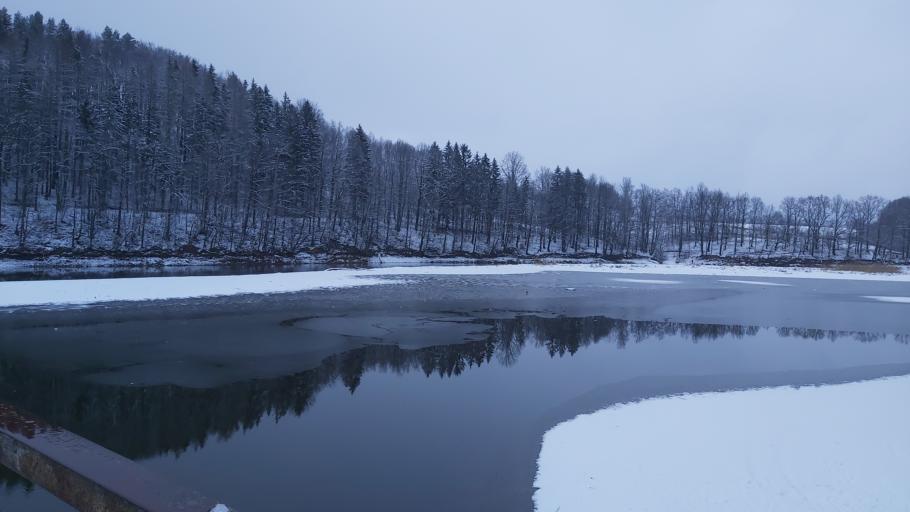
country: PL
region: Lower Silesian Voivodeship
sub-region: Powiat lwowecki
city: Gryfow Slaski
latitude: 51.0300
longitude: 15.3876
